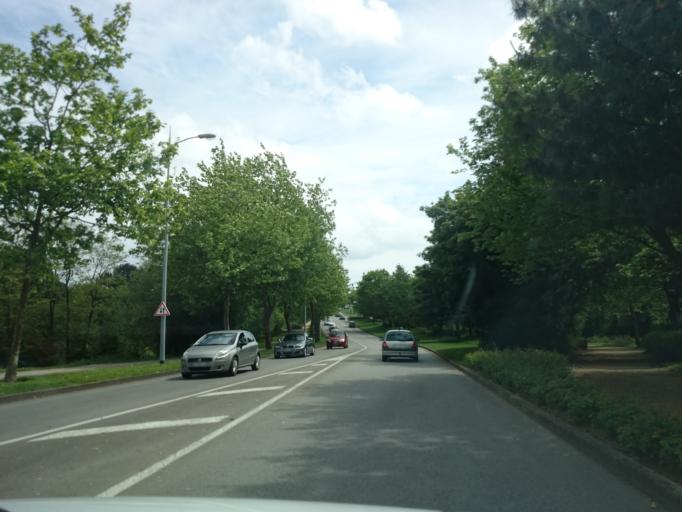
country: FR
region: Brittany
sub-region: Departement du Morbihan
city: Vannes
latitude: 47.6476
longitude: -2.7817
